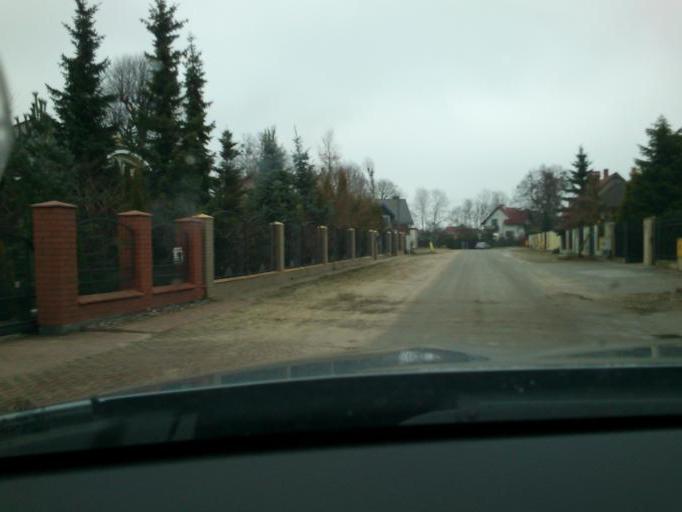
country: PL
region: Pomeranian Voivodeship
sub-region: Powiat kartuski
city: Banino
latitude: 54.3874
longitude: 18.4818
